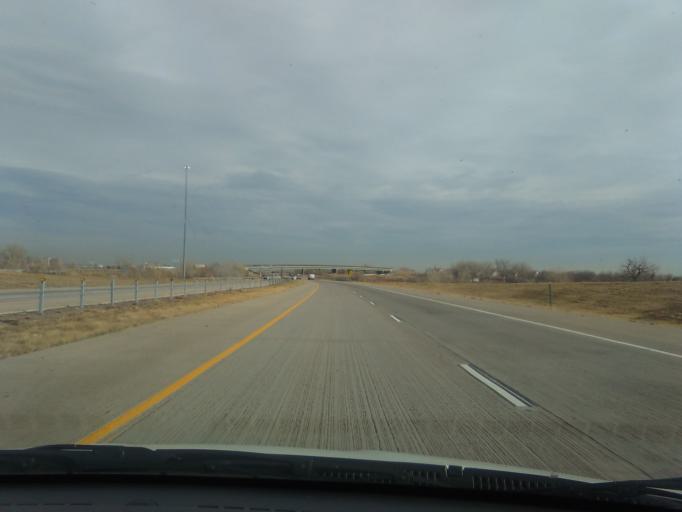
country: US
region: Colorado
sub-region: Adams County
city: Brighton
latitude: 39.9095
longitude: -104.8234
